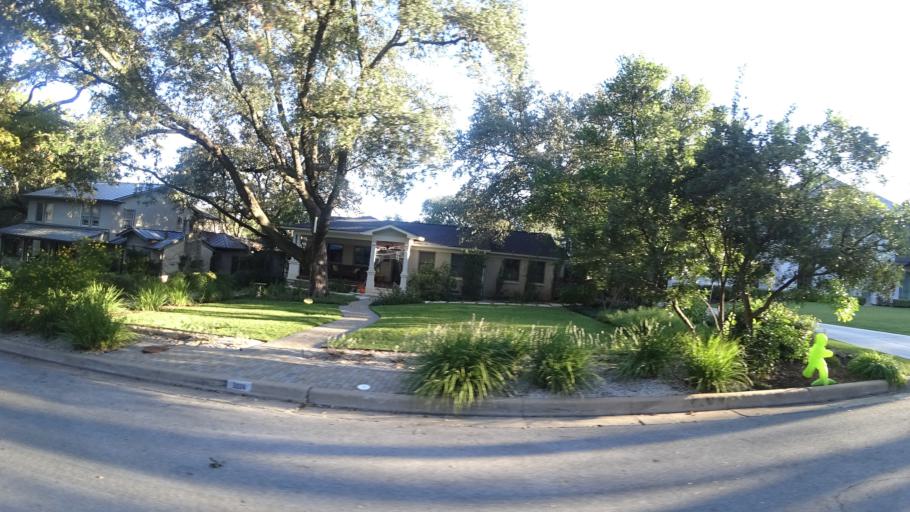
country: US
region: Texas
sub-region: Travis County
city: Rollingwood
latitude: 30.2967
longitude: -97.7741
